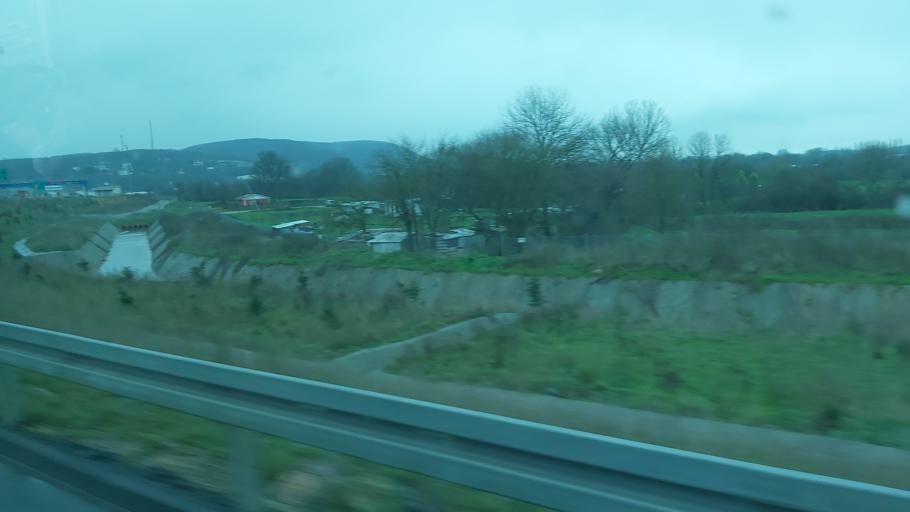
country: TR
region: Istanbul
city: Mahmut Sevket Pasa
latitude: 41.1144
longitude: 29.2930
